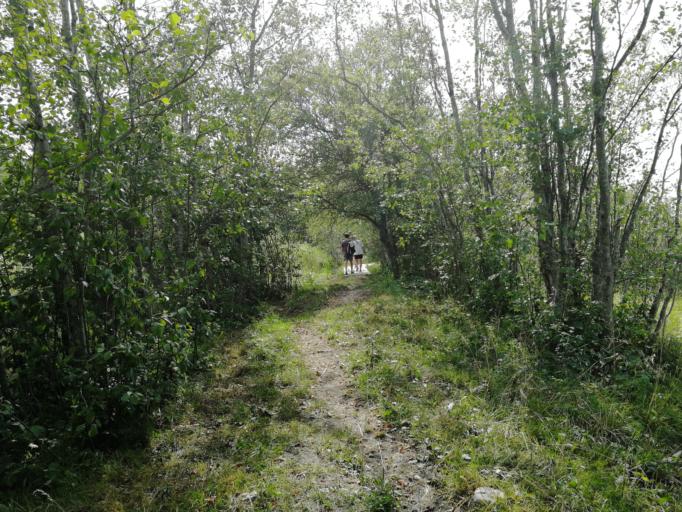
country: EE
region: Laeaene
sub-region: Lihula vald
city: Lihula
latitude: 58.7257
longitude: 23.7986
